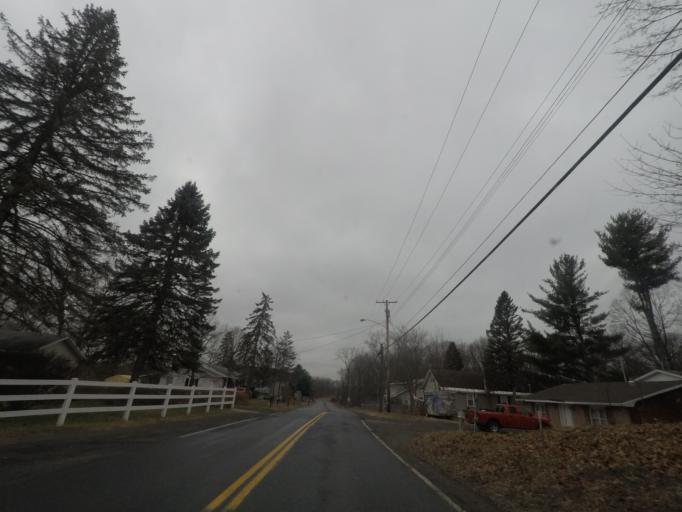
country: US
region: New York
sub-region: Saratoga County
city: Waterford
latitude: 42.7946
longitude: -73.6683
